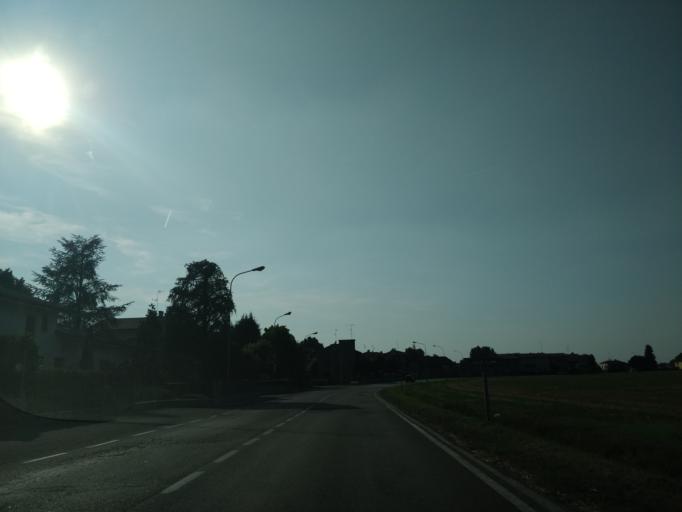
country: IT
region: Emilia-Romagna
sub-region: Provincia di Bologna
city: Castello d'Argile
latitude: 44.6817
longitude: 11.3002
